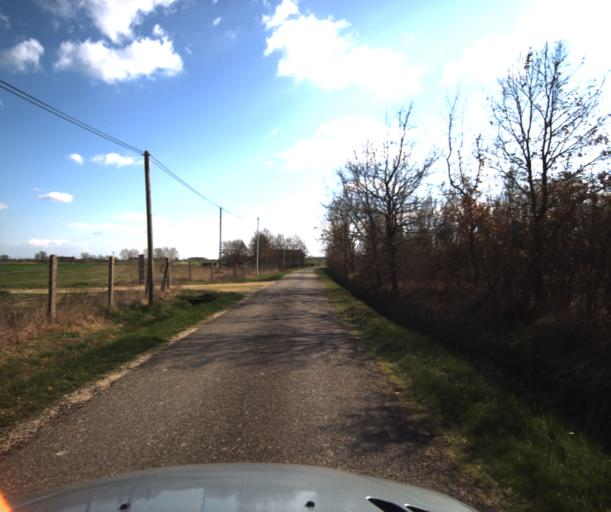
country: FR
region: Midi-Pyrenees
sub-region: Departement du Tarn-et-Garonne
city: Bressols
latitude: 43.9641
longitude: 1.2876
